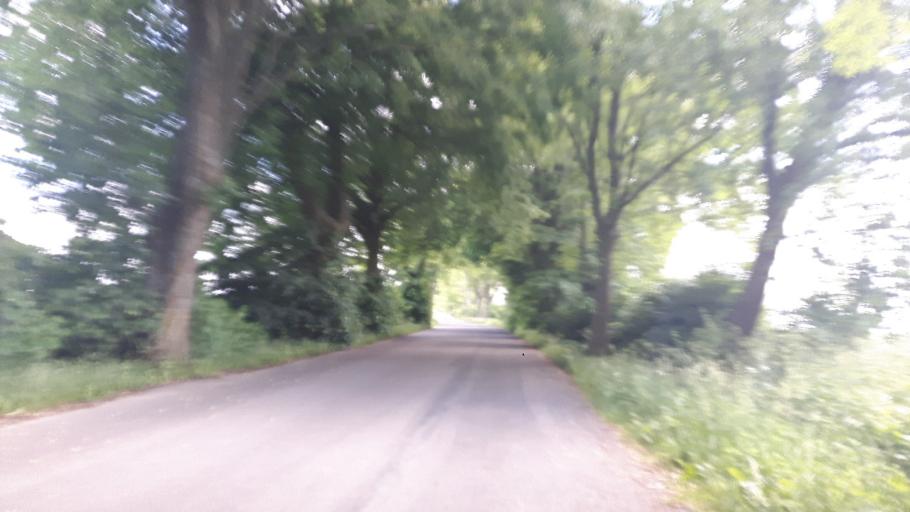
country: PL
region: West Pomeranian Voivodeship
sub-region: Powiat slawienski
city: Slawno
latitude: 54.5088
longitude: 16.5816
